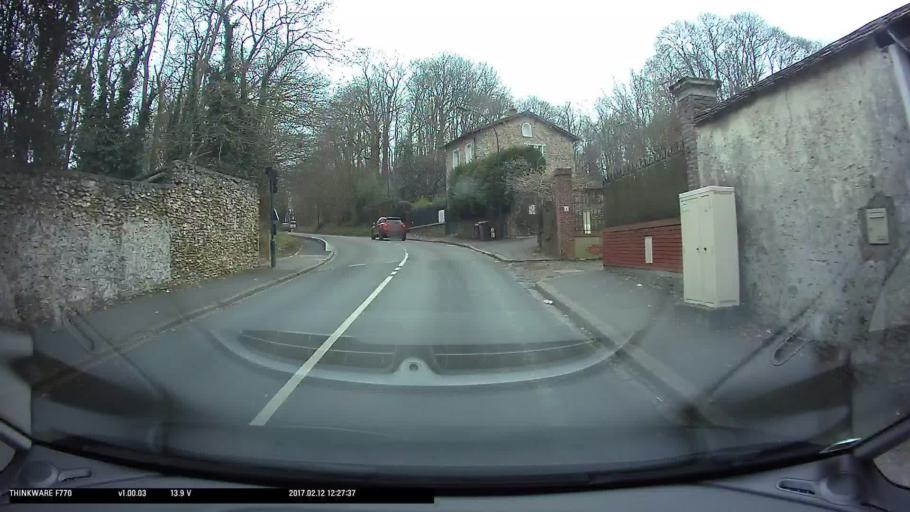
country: FR
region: Ile-de-France
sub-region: Departement du Val-d'Oise
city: Courdimanche
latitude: 49.0238
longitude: 1.9994
